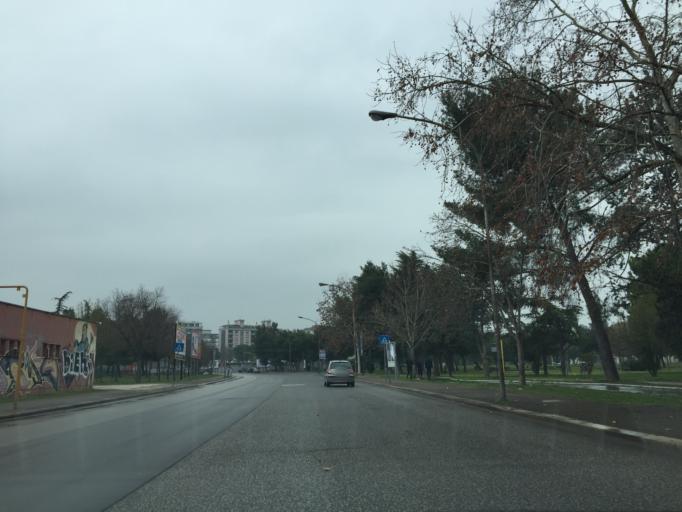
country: IT
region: Apulia
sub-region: Provincia di Foggia
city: Foggia
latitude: 41.4637
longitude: 15.5329
